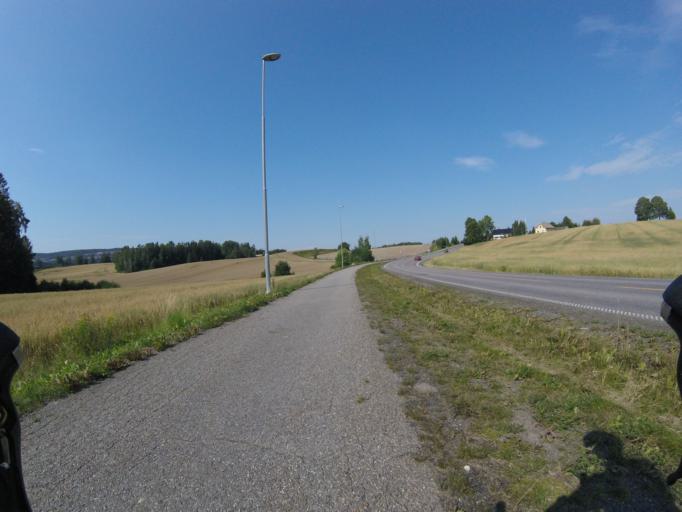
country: NO
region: Akershus
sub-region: Sorum
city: Frogner
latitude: 60.0165
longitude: 11.1119
